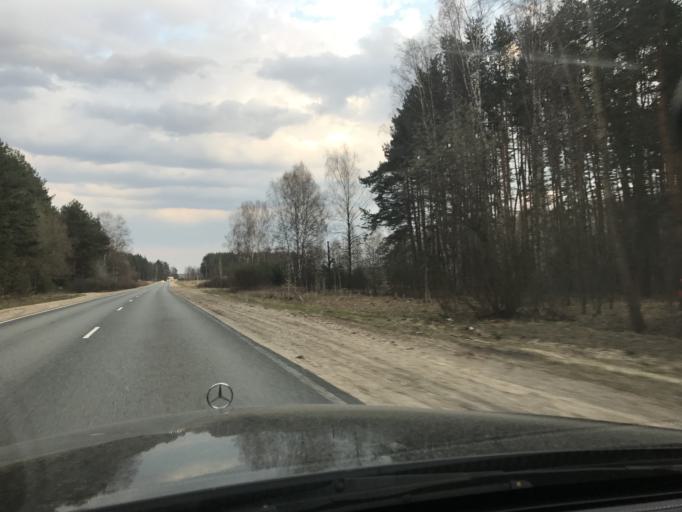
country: RU
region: Vladimir
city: Murom
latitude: 55.6357
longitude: 41.8667
